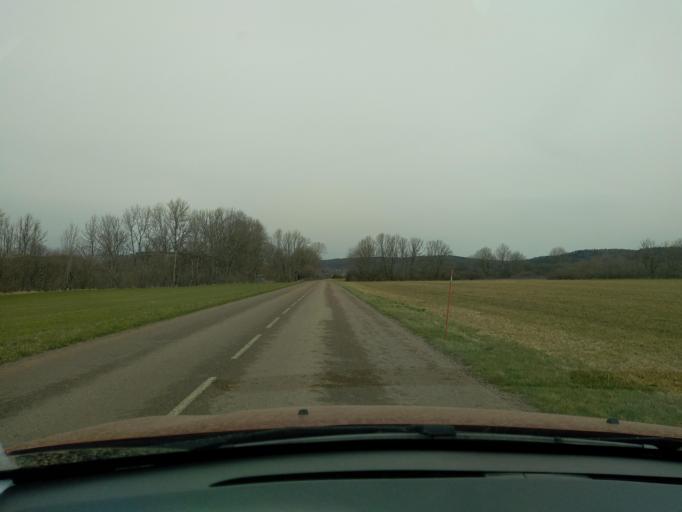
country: FR
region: Franche-Comte
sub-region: Departement du Jura
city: Clairvaux-les-Lacs
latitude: 46.5996
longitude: 5.7226
